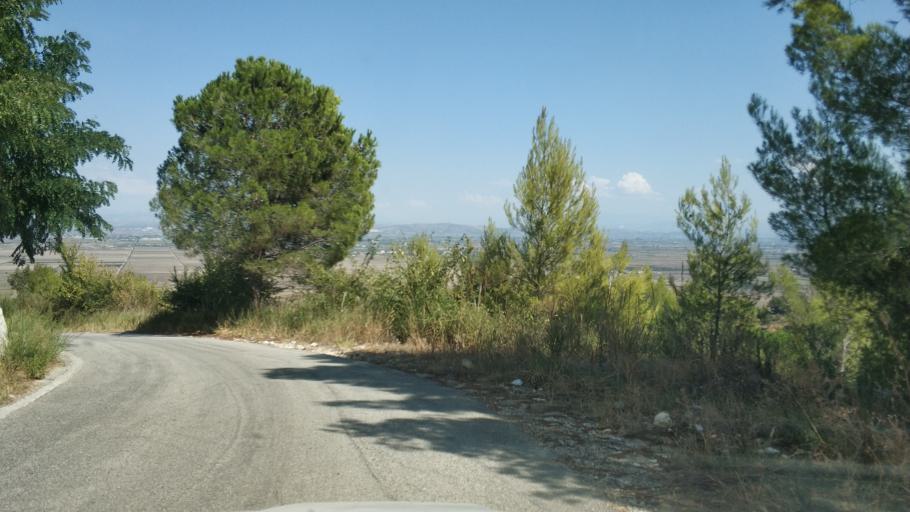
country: AL
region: Fier
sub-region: Rrethi i Lushnjes
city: Kolonje
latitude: 40.8222
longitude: 19.5962
